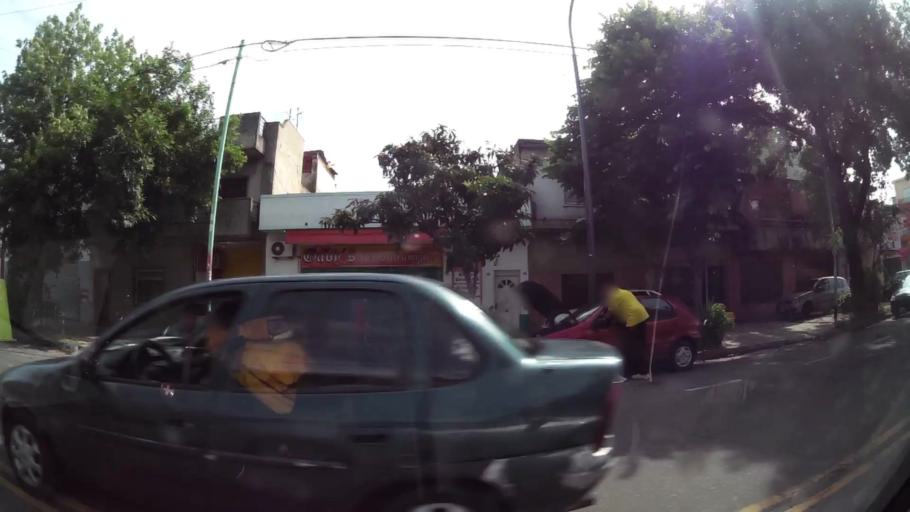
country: AR
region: Buenos Aires F.D.
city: Villa Lugano
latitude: -34.6587
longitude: -58.4352
